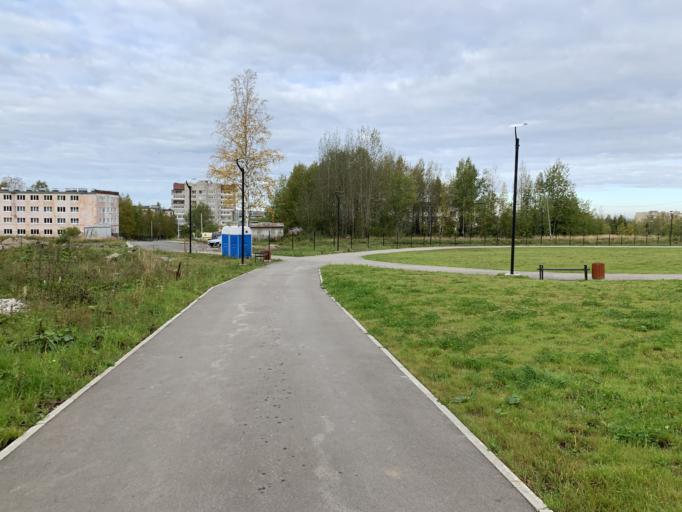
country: RU
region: Perm
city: Gubakha
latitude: 58.8322
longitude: 57.5625
